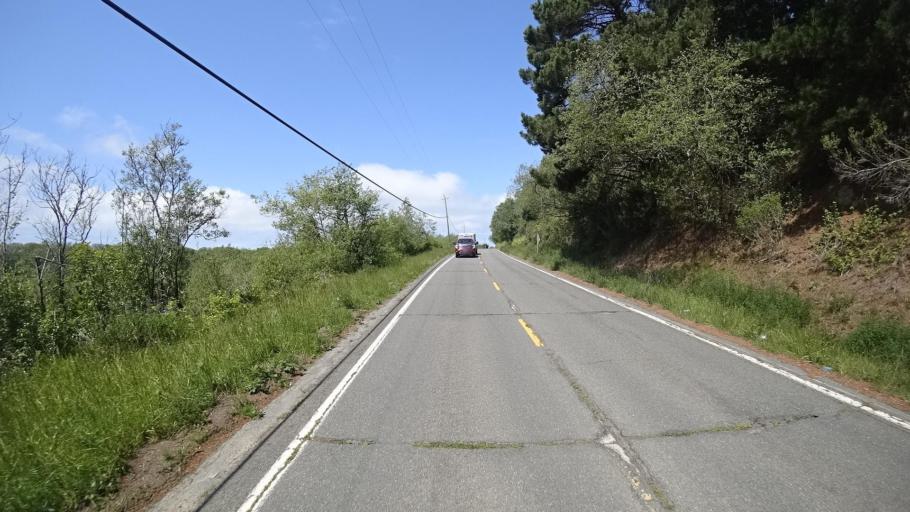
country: US
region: California
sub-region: Humboldt County
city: Ferndale
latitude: 40.6242
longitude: -124.2183
